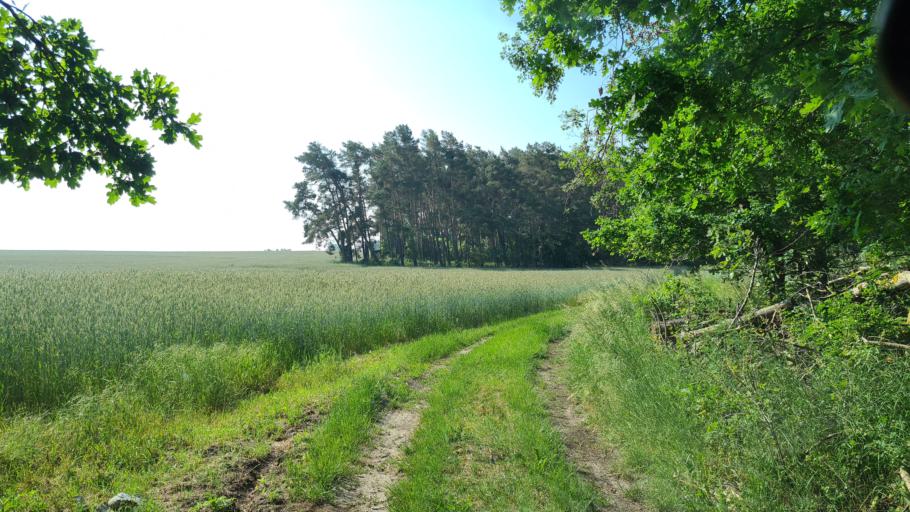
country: DE
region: Brandenburg
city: Hohenbucko
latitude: 51.6981
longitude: 13.5077
